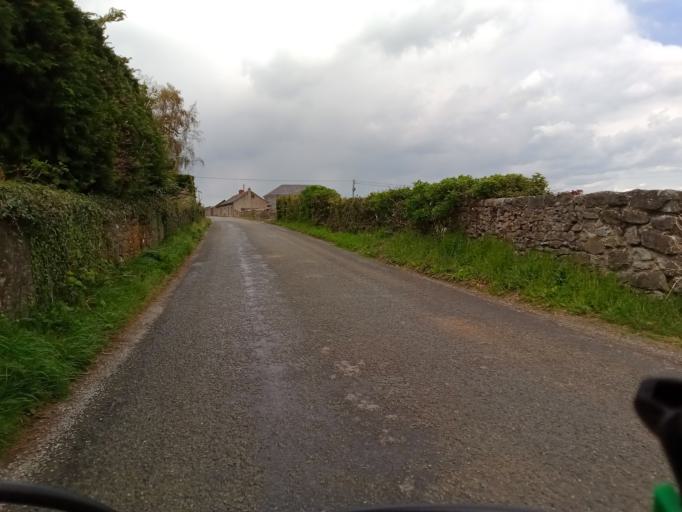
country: IE
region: Leinster
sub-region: Kilkenny
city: Kilkenny
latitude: 52.6353
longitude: -7.2747
